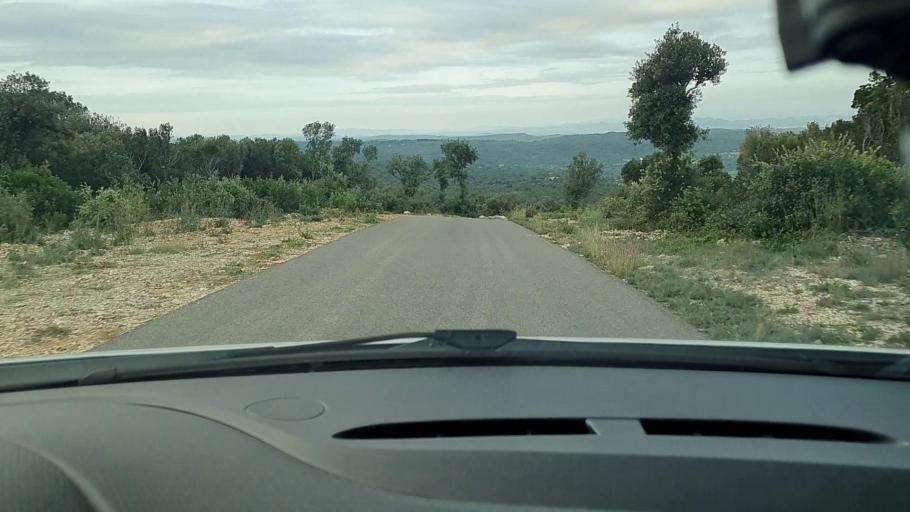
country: FR
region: Languedoc-Roussillon
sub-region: Departement du Gard
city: Mons
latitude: 44.1413
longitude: 4.2625
